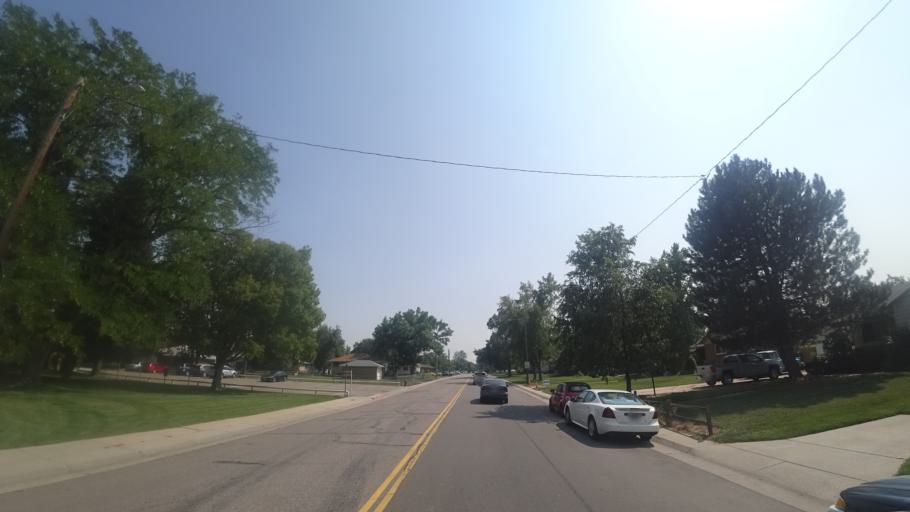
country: US
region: Colorado
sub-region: Arapahoe County
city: Englewood
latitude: 39.6264
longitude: -104.9833
